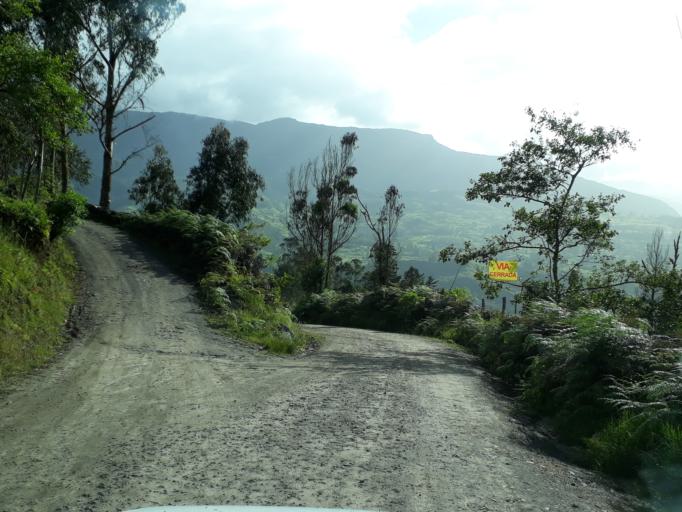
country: CO
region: Cundinamarca
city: Junin
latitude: 4.7838
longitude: -73.6832
